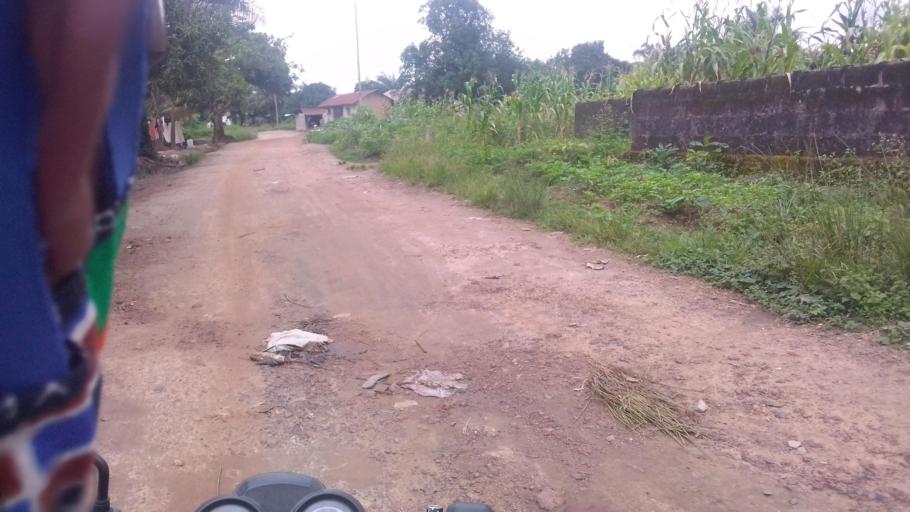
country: SL
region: Eastern Province
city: Kenema
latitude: 7.8632
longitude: -11.1729
